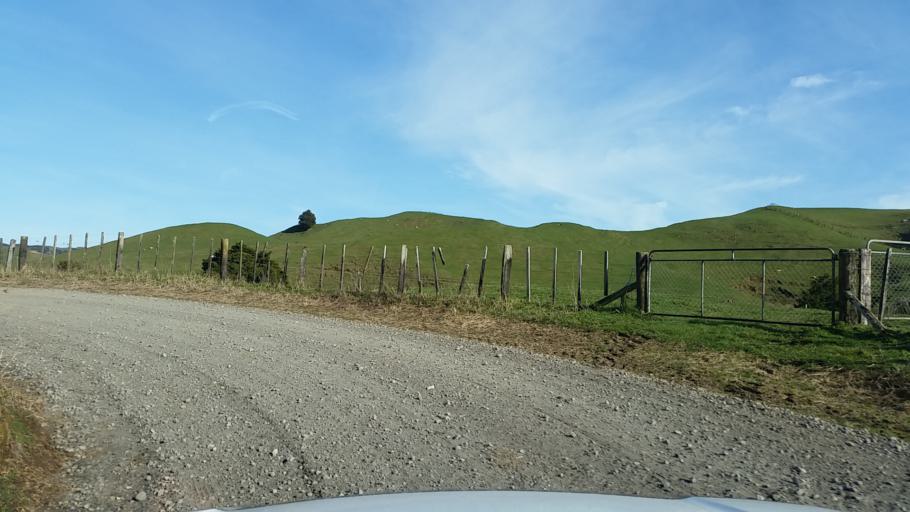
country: NZ
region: Taranaki
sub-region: South Taranaki District
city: Eltham
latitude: -39.3139
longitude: 174.5351
